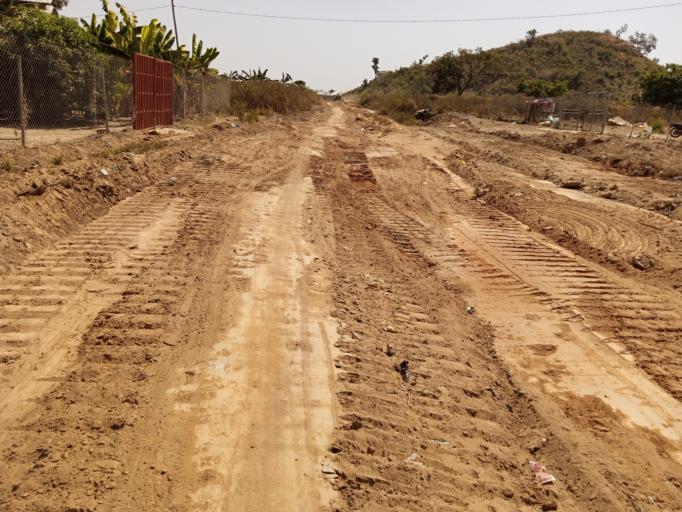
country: NG
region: Abuja Federal Capital Territory
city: Kuje
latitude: 8.9056
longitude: 7.3371
